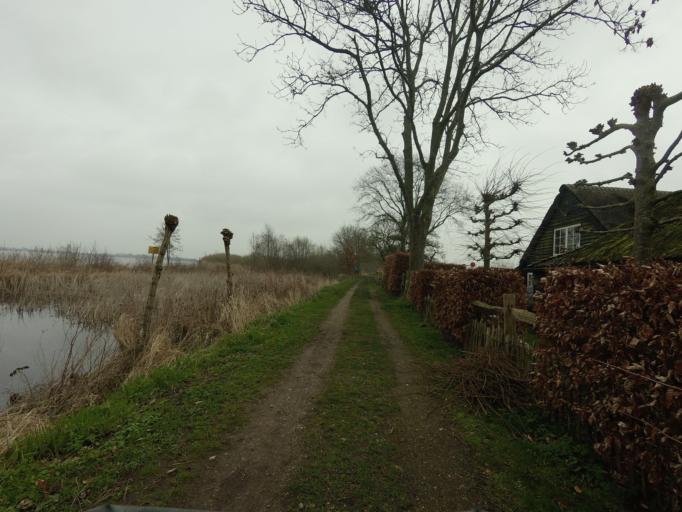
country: NL
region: North Holland
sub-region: Gemeente Wijdemeren
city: Oud-Loosdrecht
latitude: 52.1730
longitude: 5.0793
